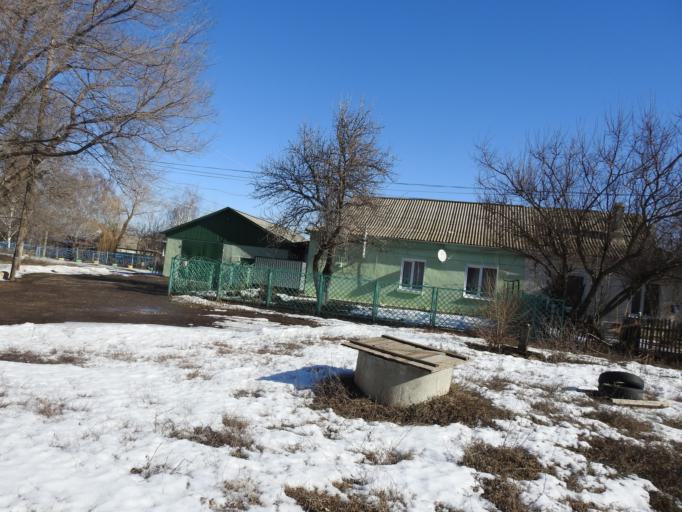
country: RU
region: Saratov
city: Yershov
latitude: 51.3403
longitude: 48.2247
